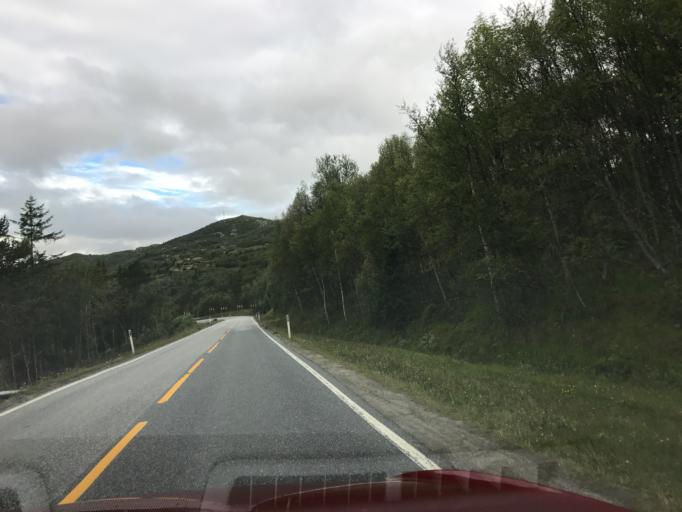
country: NO
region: Buskerud
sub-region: Al
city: Al
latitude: 60.3255
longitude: 8.5081
